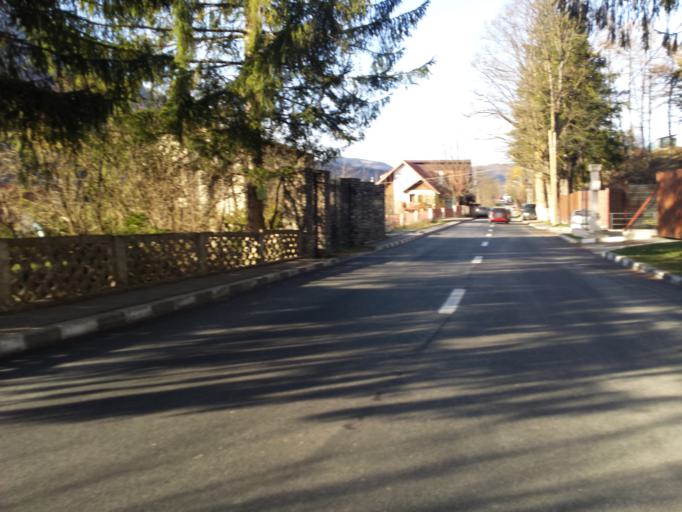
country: RO
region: Prahova
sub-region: Oras Busteni
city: Busteni
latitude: 45.4039
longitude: 25.5402
